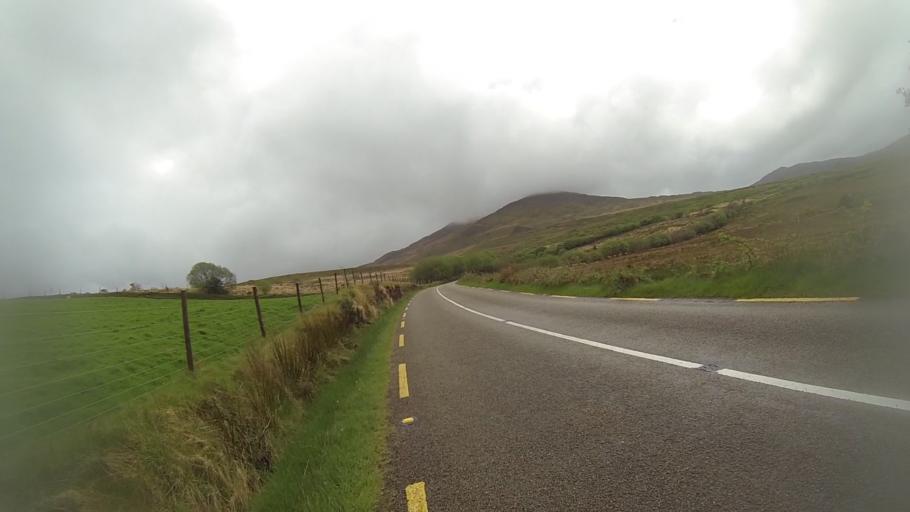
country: IE
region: Munster
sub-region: Ciarrai
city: Kenmare
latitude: 51.8831
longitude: -9.7863
